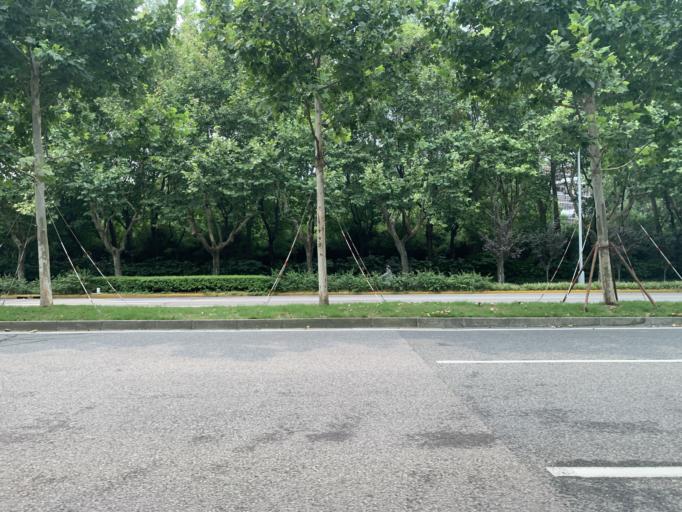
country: CN
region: Shanghai Shi
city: Huamu
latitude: 31.2204
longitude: 121.5430
